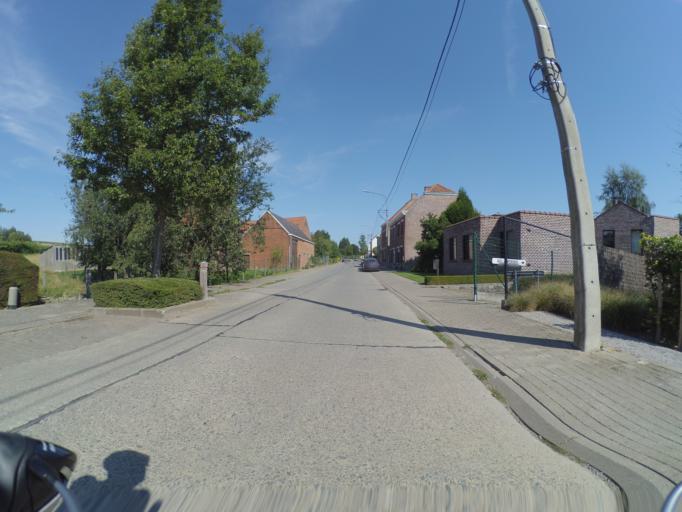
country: BE
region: Flanders
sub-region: Provincie Oost-Vlaanderen
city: Oudenaarde
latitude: 50.7984
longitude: 3.6211
